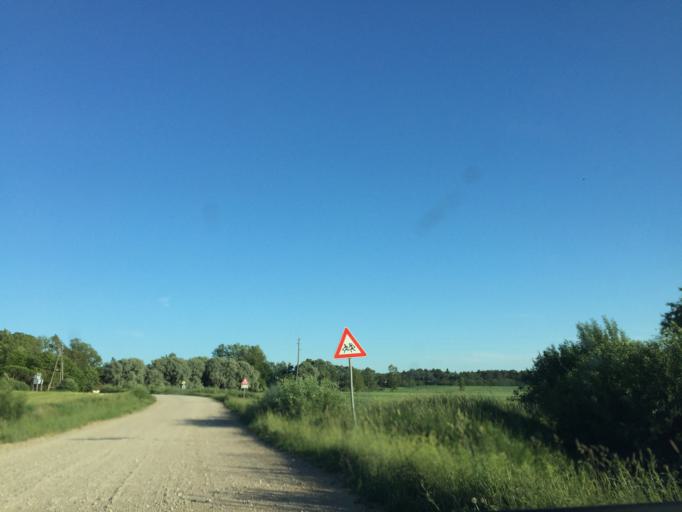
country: LV
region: Broceni
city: Broceni
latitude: 56.7868
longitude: 22.5612
